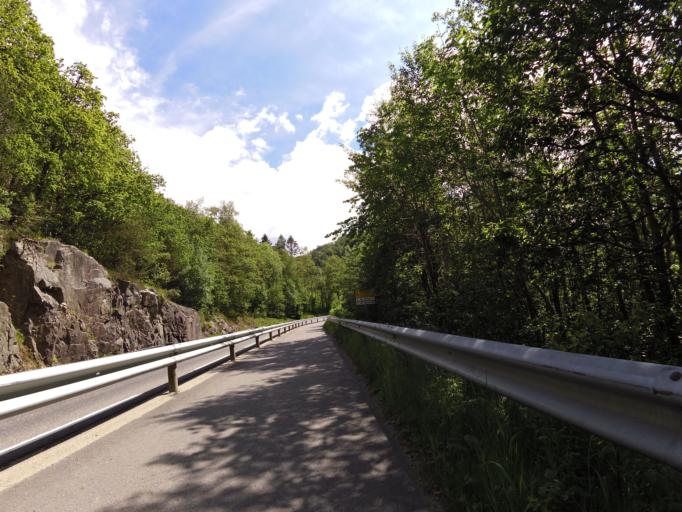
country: NO
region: Vest-Agder
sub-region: Lyngdal
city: Lyngdal
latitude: 58.1166
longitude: 7.0630
